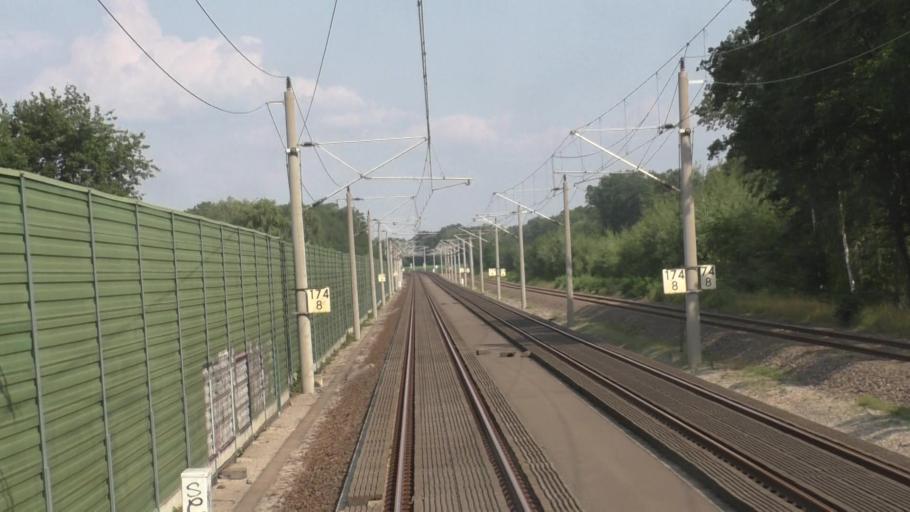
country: DE
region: Brandenburg
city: Rathenow
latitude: 52.5910
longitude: 12.2984
